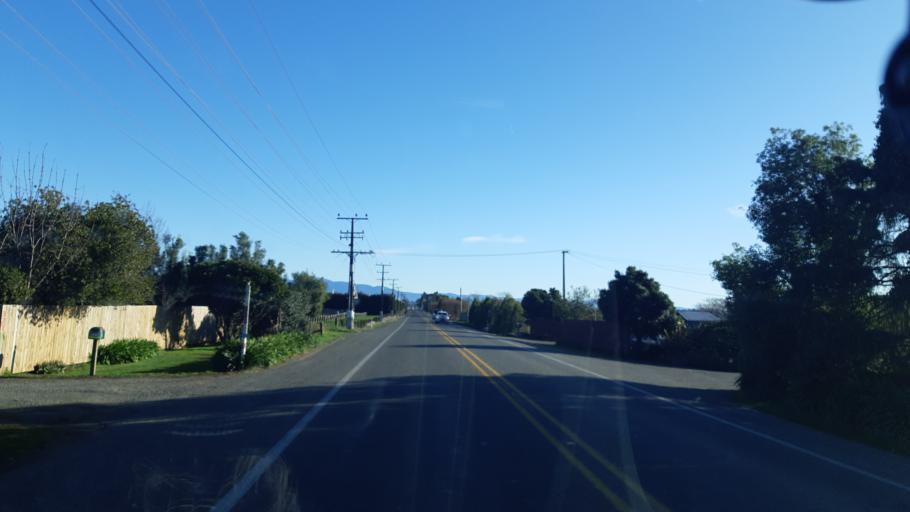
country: NZ
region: Tasman
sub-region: Tasman District
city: Richmond
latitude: -41.3236
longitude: 173.1436
